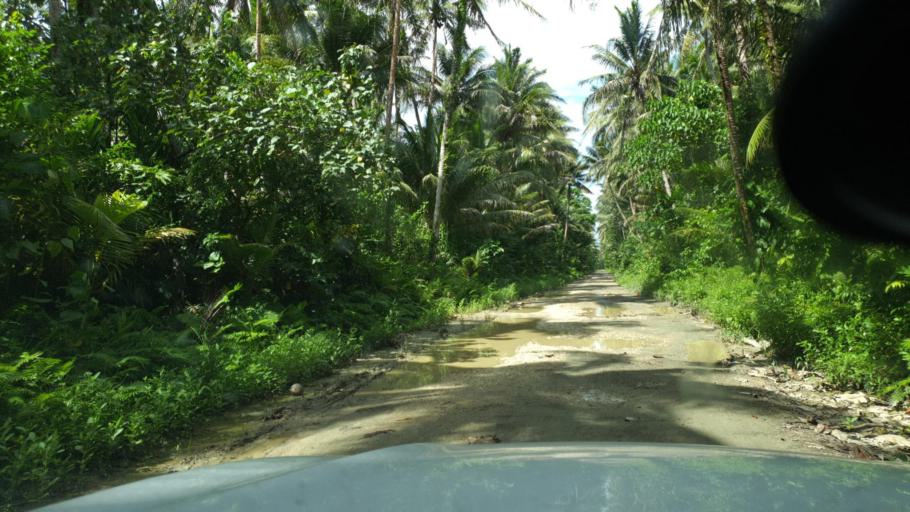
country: SB
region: Central Province
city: Tulaghi
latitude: -9.4621
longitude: 160.4205
